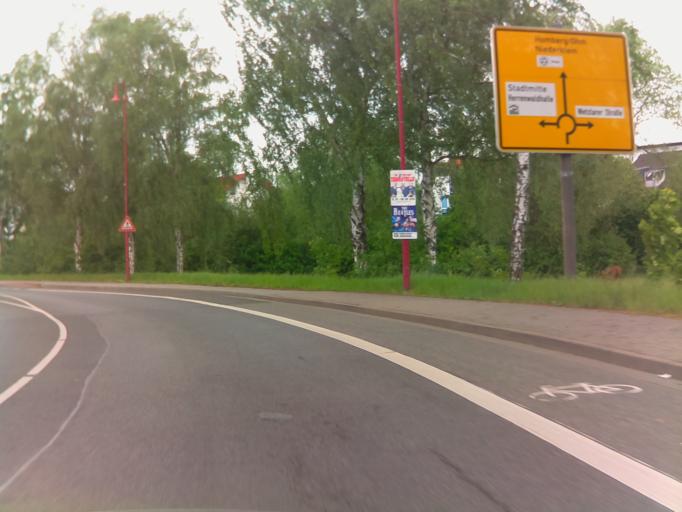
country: DE
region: Hesse
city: Stadtallendorf
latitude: 50.8302
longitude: 9.0126
